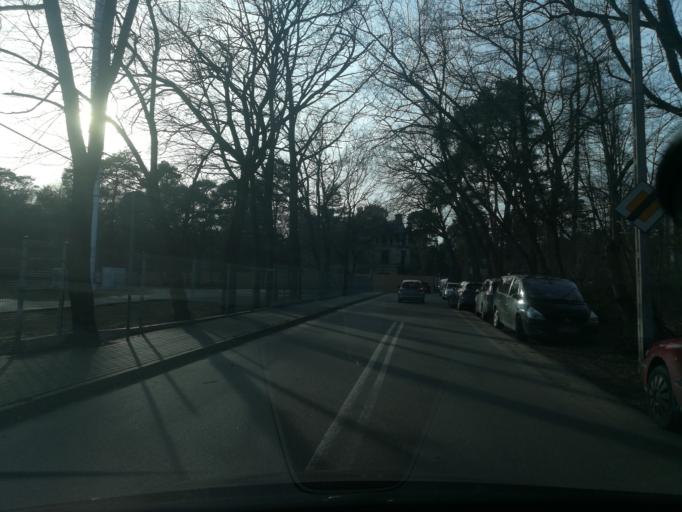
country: PL
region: Masovian Voivodeship
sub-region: Powiat piaseczynski
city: Konstancin-Jeziorna
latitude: 52.0831
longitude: 21.1117
